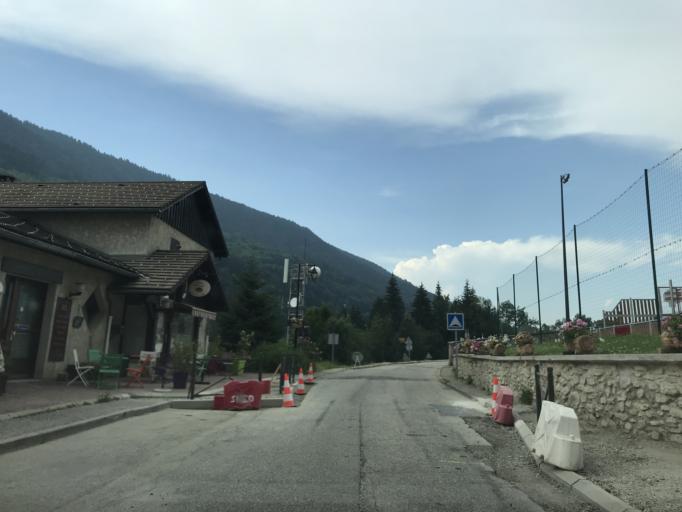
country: FR
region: Rhone-Alpes
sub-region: Departement de l'Isere
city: Allevard
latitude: 45.3203
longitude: 6.0866
